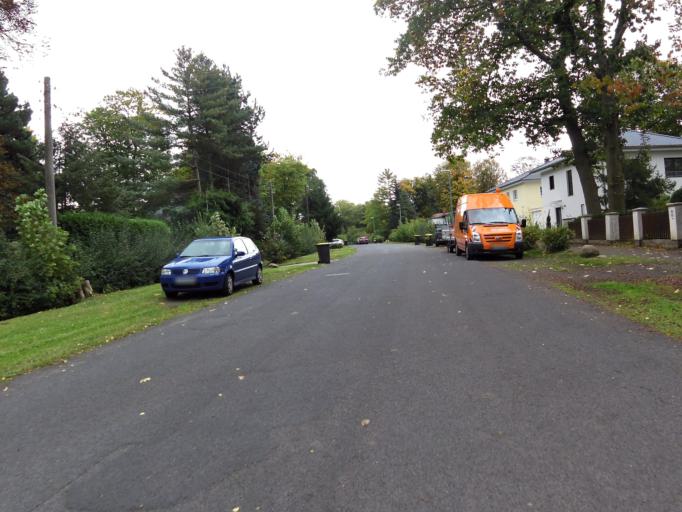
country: DE
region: Saxony
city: Grossposna
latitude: 51.3146
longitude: 12.4489
